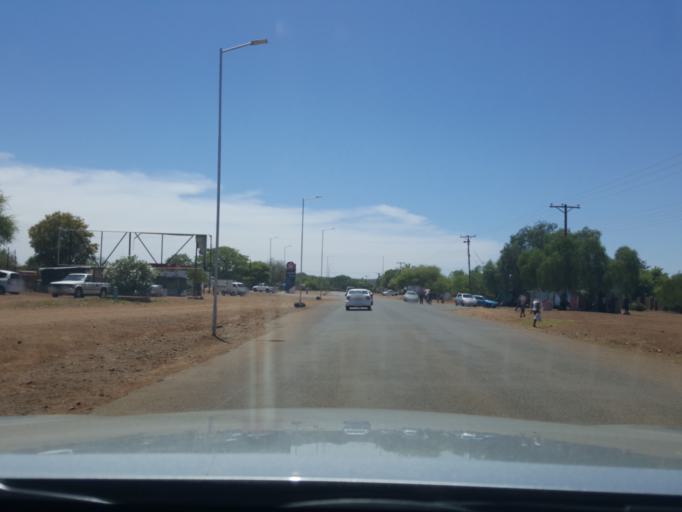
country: BW
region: South East
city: Ramotswa
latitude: -24.8652
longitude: 25.8625
